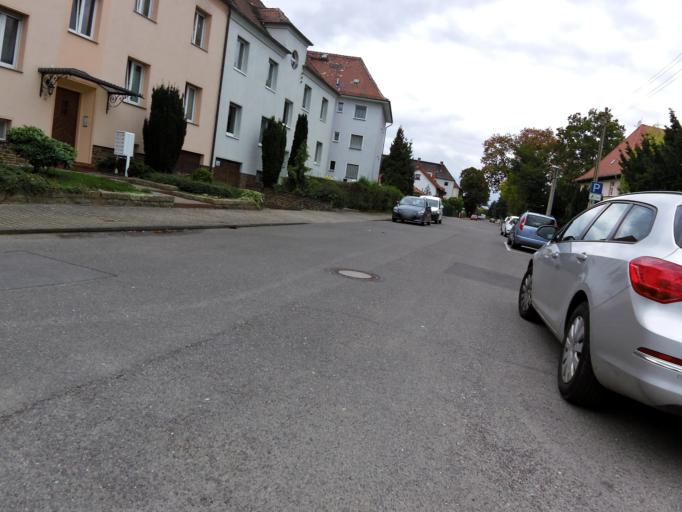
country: DE
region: Saxony
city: Grossposna
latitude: 51.3108
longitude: 12.4587
